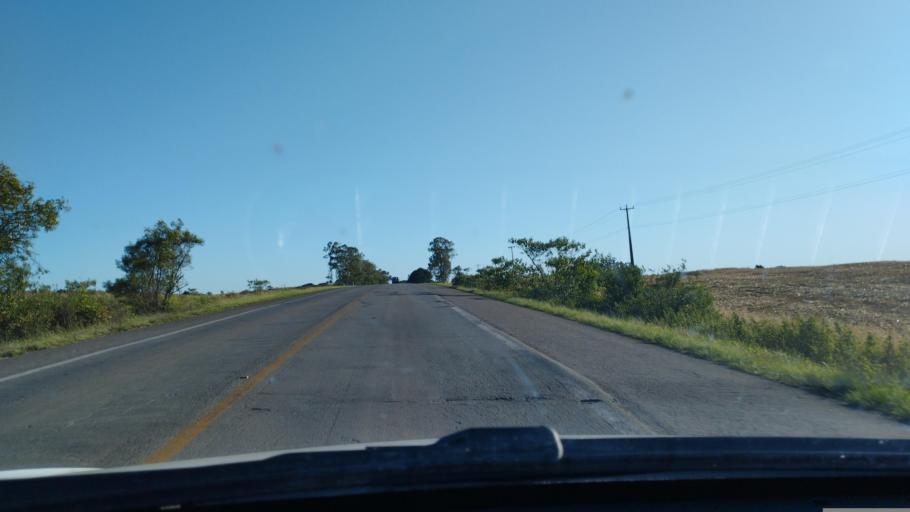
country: BR
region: Rio Grande do Sul
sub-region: Julio De Castilhos
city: Julio de Castilhos
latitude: -29.4258
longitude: -53.6737
